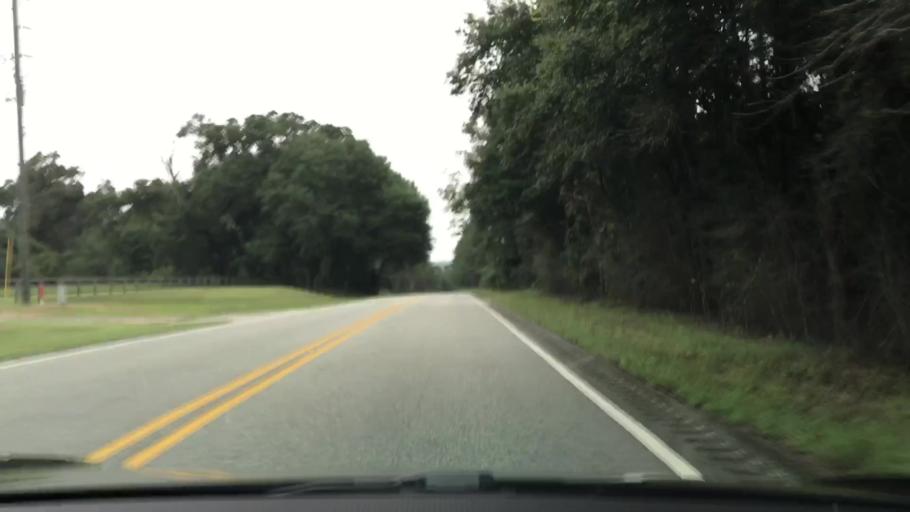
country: US
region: Alabama
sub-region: Coffee County
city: Elba
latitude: 31.3674
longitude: -86.1070
